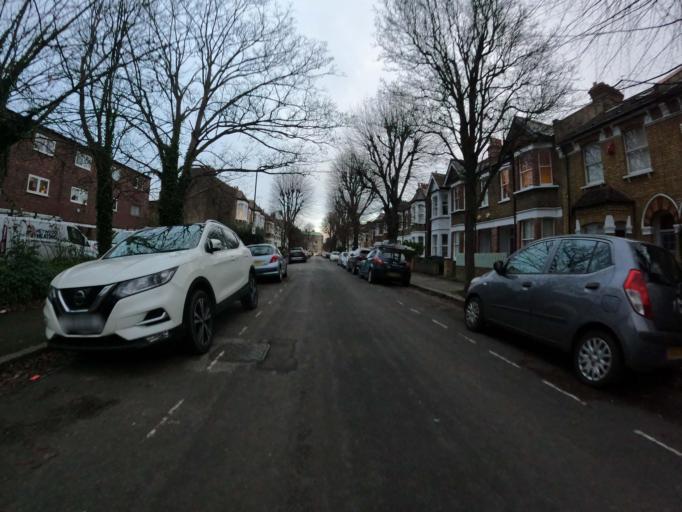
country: GB
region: England
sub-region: Greater London
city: Acton
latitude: 51.4999
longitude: -0.2664
